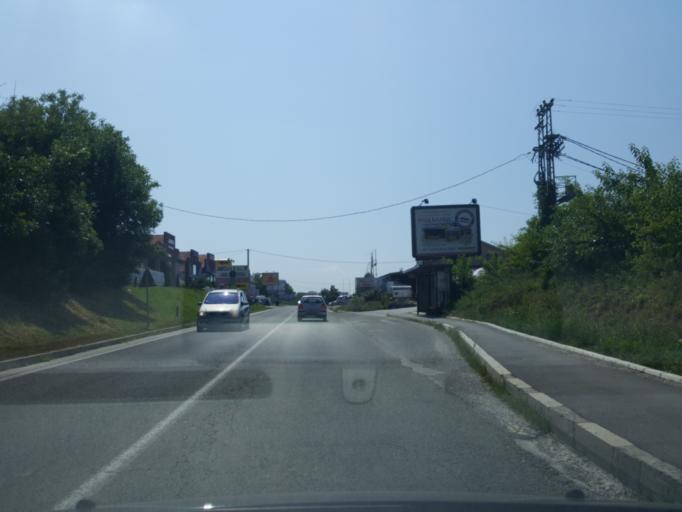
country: RS
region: Central Serbia
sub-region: Belgrade
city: Mladenovac
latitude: 44.4610
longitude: 20.6708
